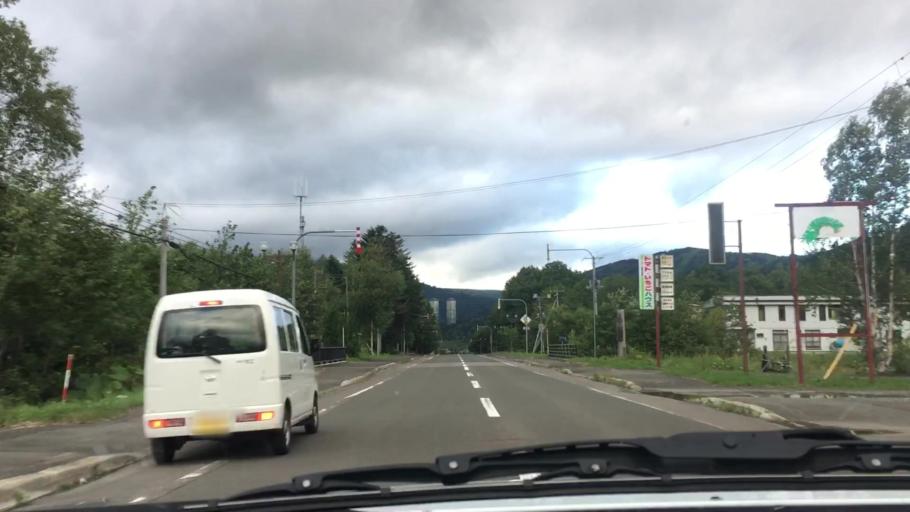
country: JP
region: Hokkaido
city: Shimo-furano
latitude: 43.0438
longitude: 142.6539
